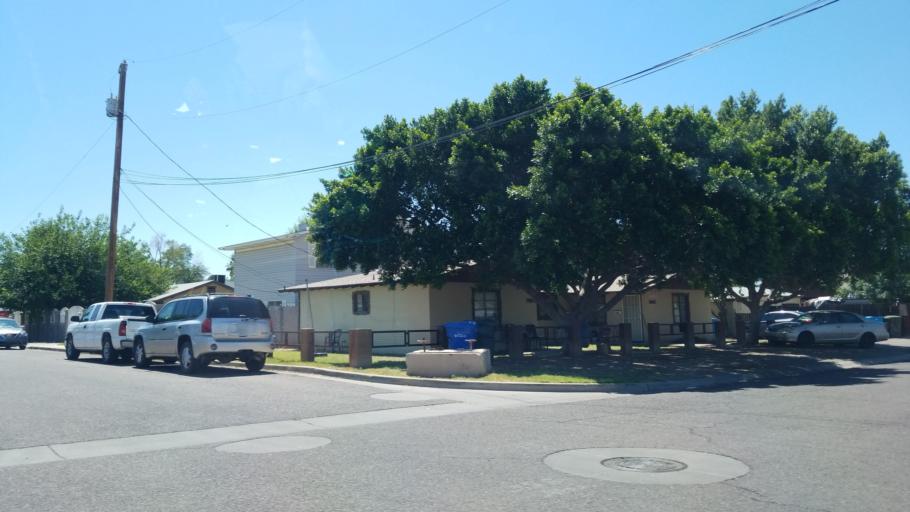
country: US
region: Arizona
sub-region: Maricopa County
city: Phoenix
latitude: 33.5057
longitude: -112.0869
